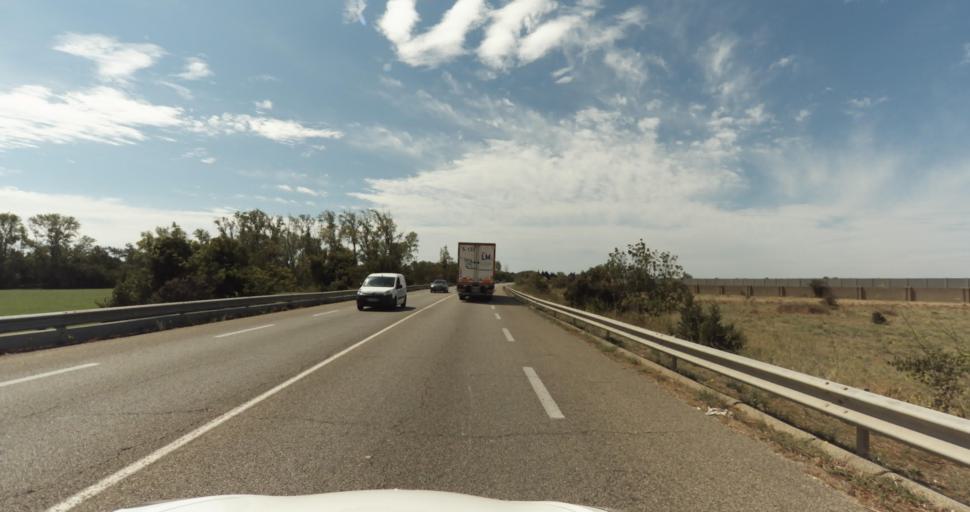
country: FR
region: Provence-Alpes-Cote d'Azur
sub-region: Departement des Bouches-du-Rhone
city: Miramas
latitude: 43.5753
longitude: 4.9841
